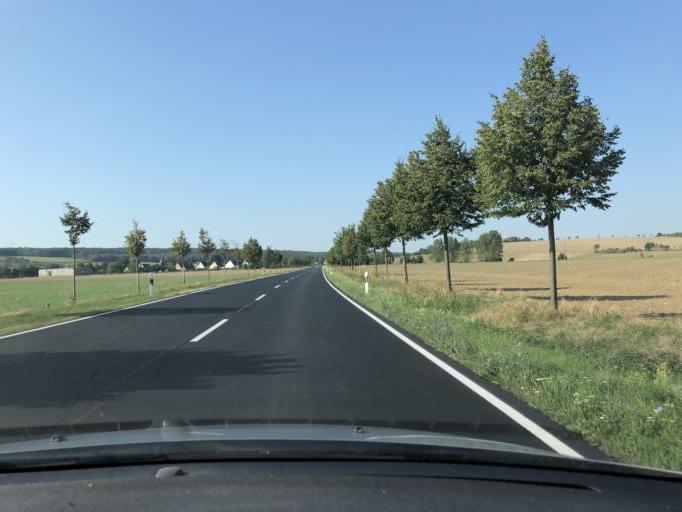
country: DE
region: Saxony-Anhalt
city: Goseck
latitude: 51.2431
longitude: 11.8331
